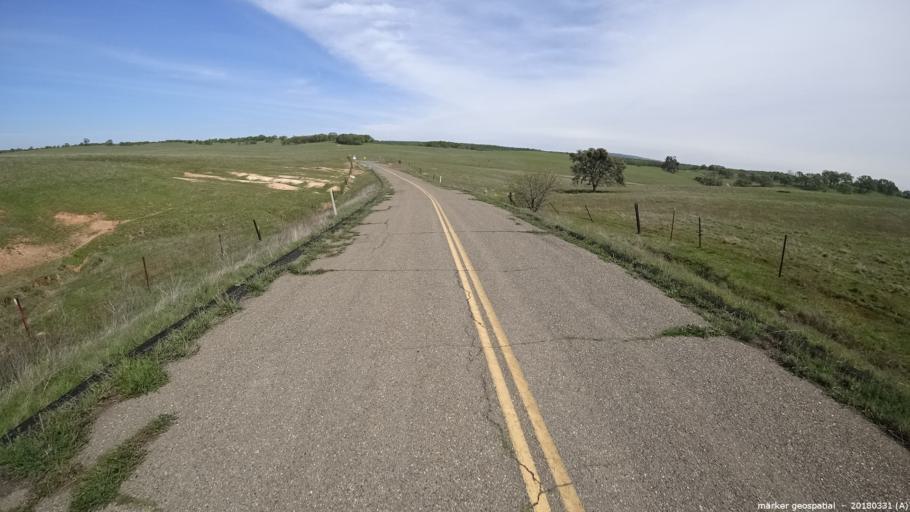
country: US
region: California
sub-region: Sacramento County
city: Rancho Murieta
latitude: 38.5554
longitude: -121.1197
